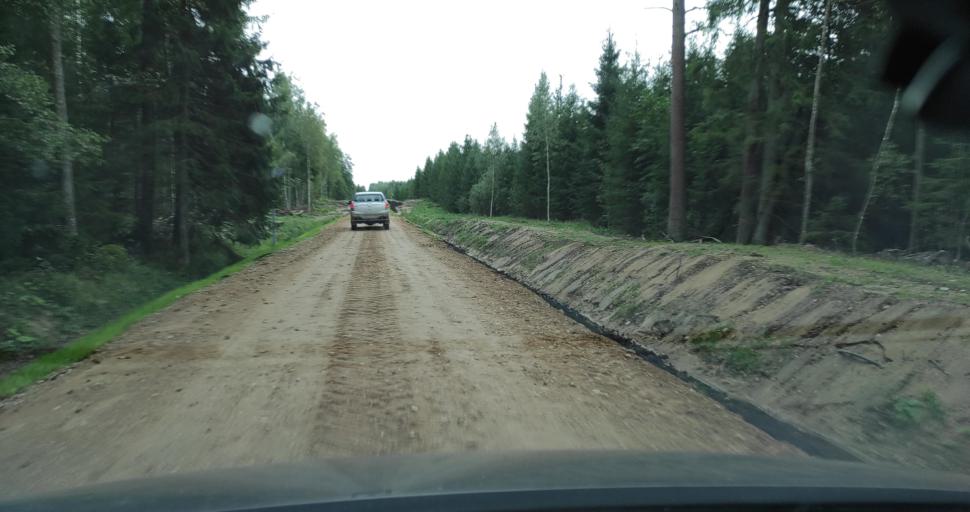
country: LV
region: Talsu Rajons
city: Sabile
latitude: 57.0203
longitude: 22.3529
